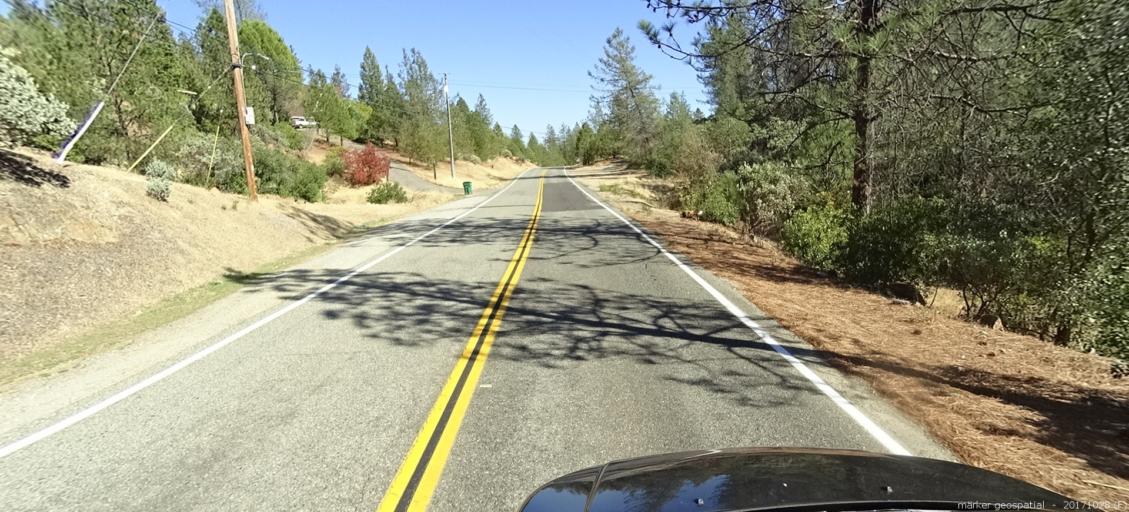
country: US
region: California
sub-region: Shasta County
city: Shasta
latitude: 40.6185
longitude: -122.4765
